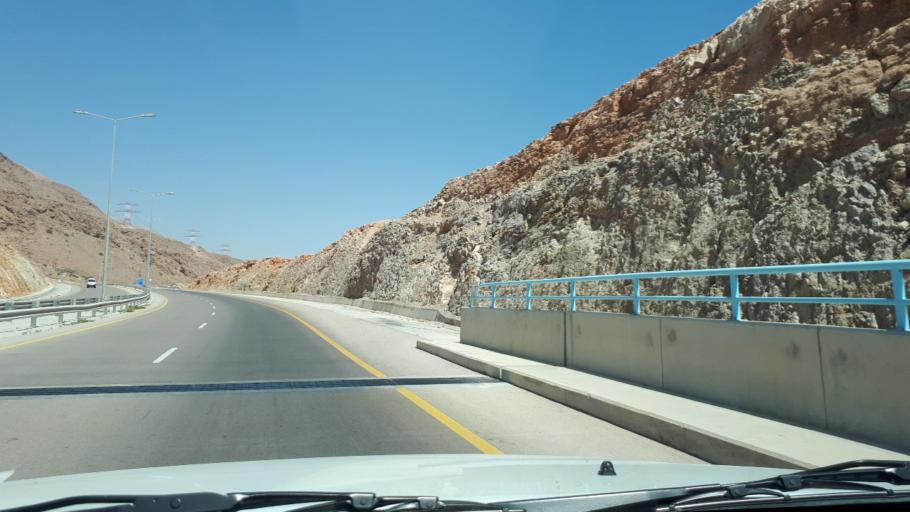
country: OM
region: Ash Sharqiyah
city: Sur
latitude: 22.8235
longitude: 59.2585
